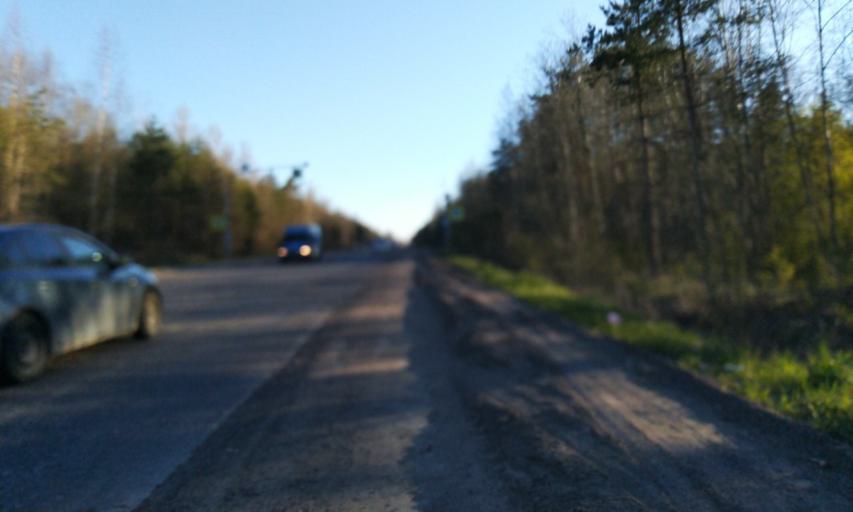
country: RU
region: Leningrad
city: Toksovo
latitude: 60.1284
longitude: 30.5186
